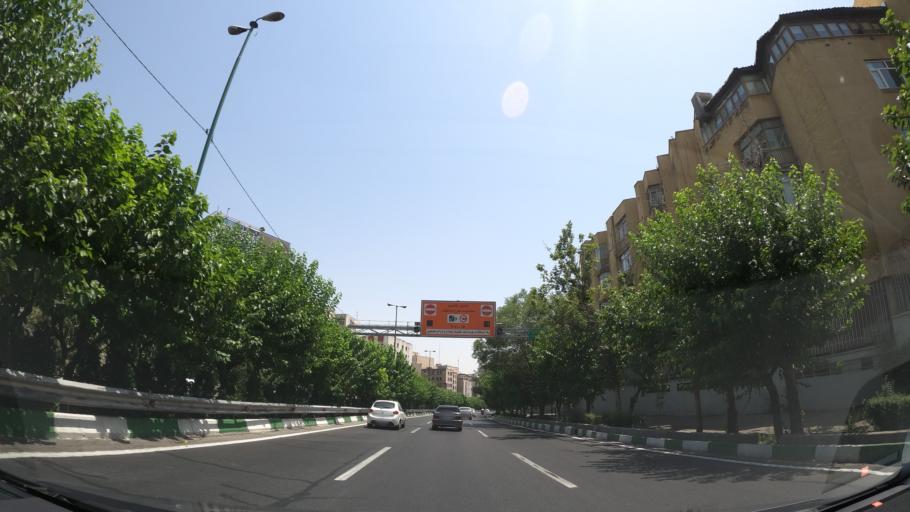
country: IR
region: Tehran
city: Tehran
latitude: 35.7271
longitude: 51.4235
